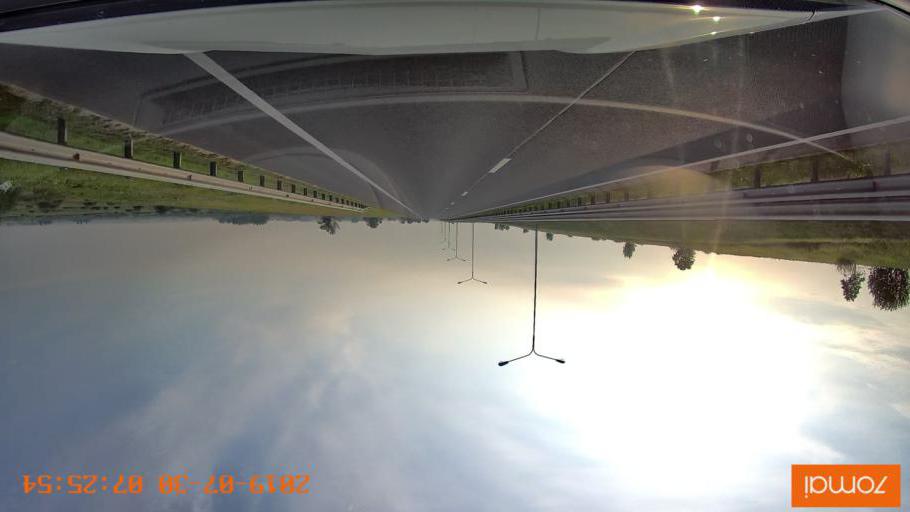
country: RU
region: Kaliningrad
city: Gvardeysk
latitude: 54.6844
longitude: 20.8464
